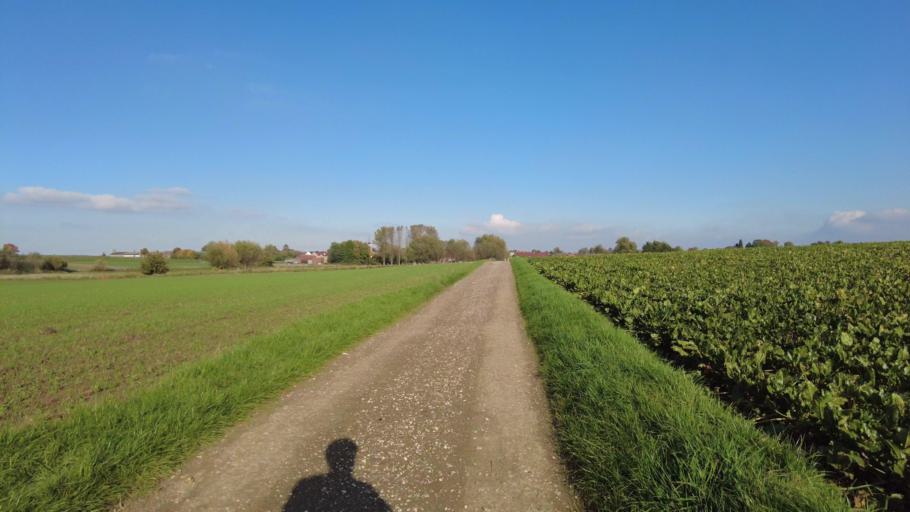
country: BE
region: Wallonia
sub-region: Province du Brabant Wallon
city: Jodoigne
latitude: 50.7348
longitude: 4.8896
